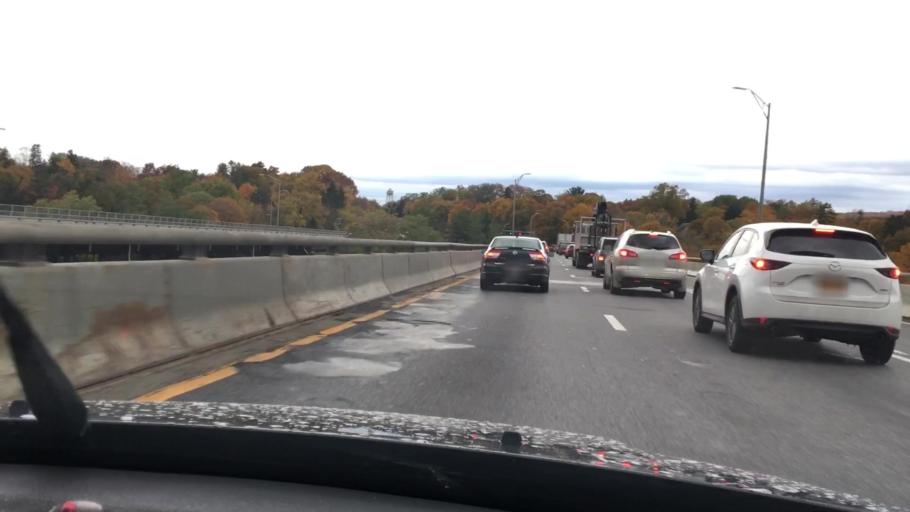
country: US
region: New York
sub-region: Orange County
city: Balmville
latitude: 41.5209
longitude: -74.0064
